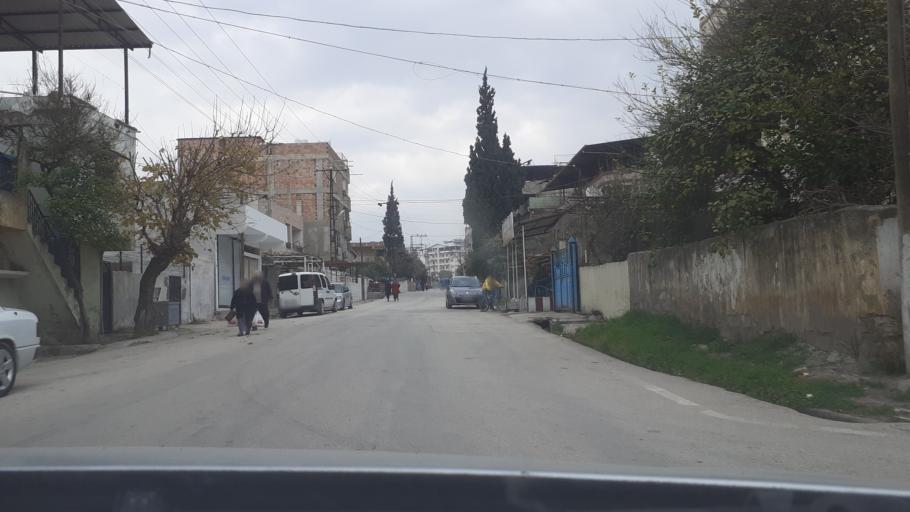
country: TR
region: Hatay
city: Kirikhan
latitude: 36.4946
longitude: 36.3510
